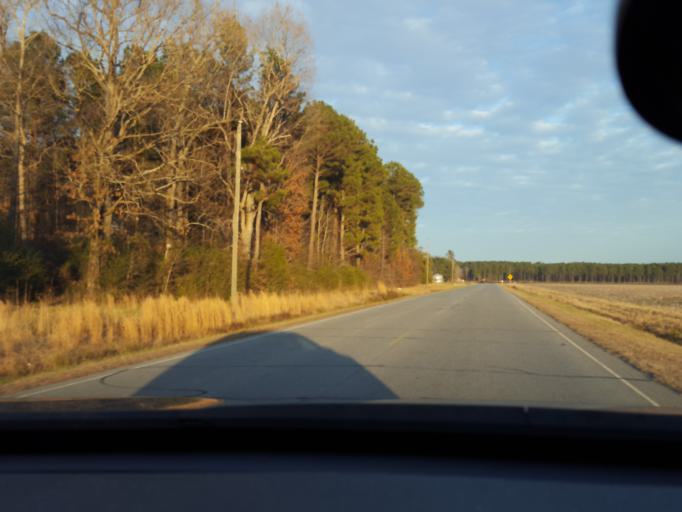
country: US
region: North Carolina
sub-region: Hertford County
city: Murfreesboro
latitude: 36.2758
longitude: -77.2128
